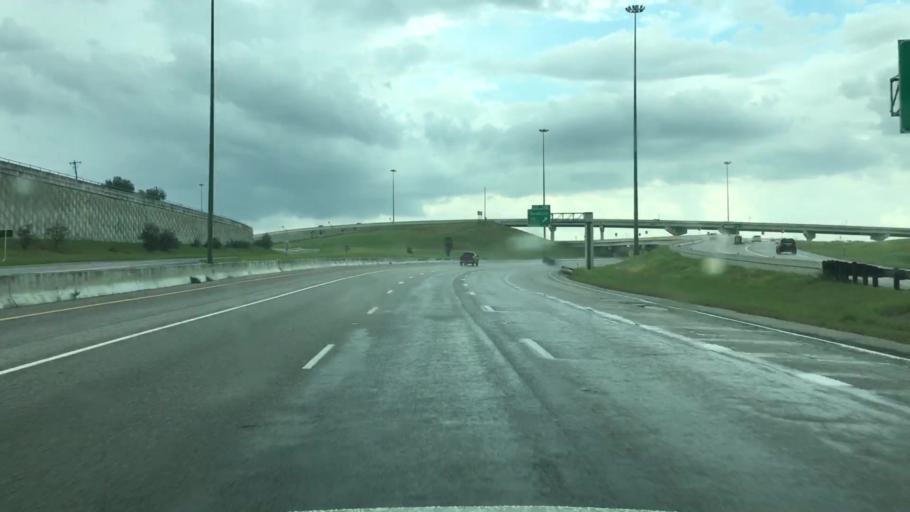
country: US
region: Texas
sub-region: Nueces County
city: Robstown
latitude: 27.8622
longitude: -97.6188
